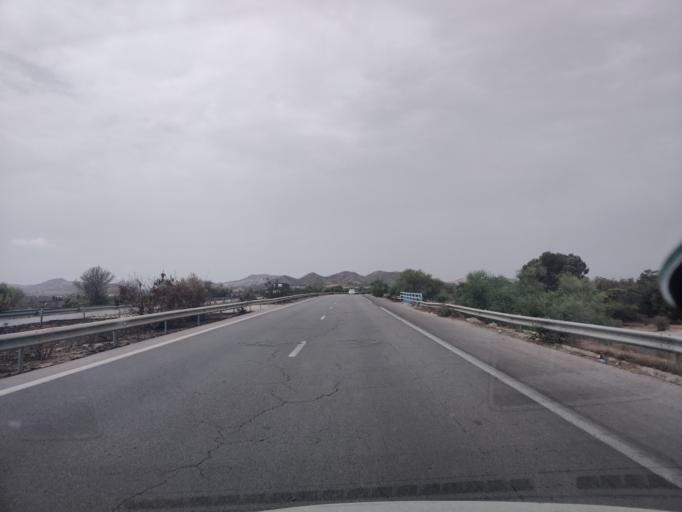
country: TN
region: Susah
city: Harqalah
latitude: 36.2129
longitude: 10.4236
